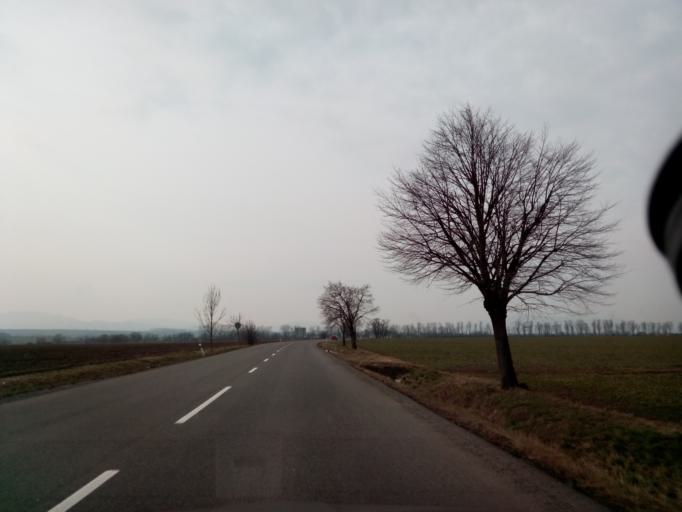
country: SK
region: Kosicky
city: Trebisov
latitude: 48.5492
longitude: 21.6884
